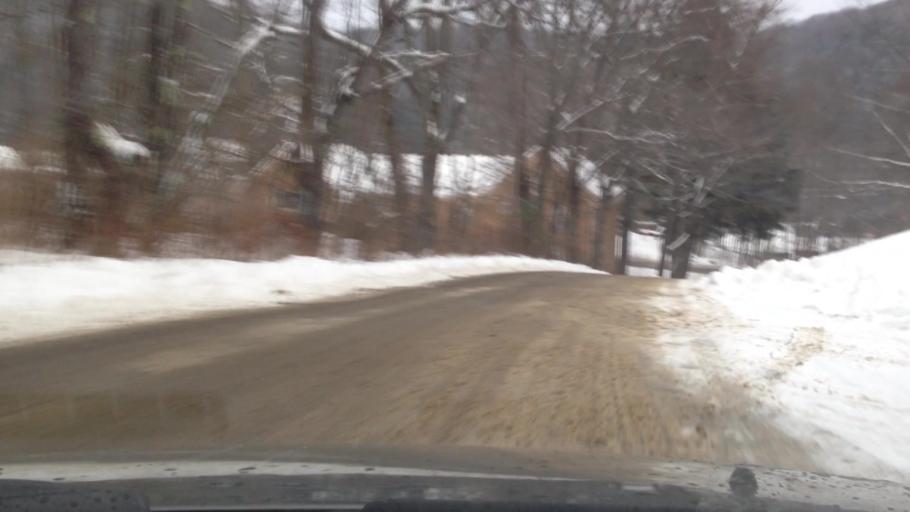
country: US
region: New Hampshire
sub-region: Cheshire County
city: Keene
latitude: 43.0489
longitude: -72.2590
